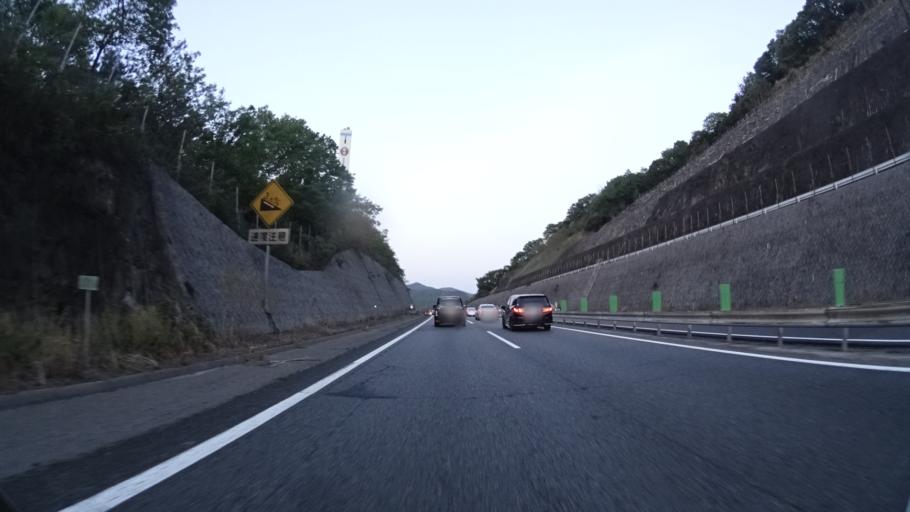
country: JP
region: Hyogo
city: Kariya
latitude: 34.7790
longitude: 134.2333
